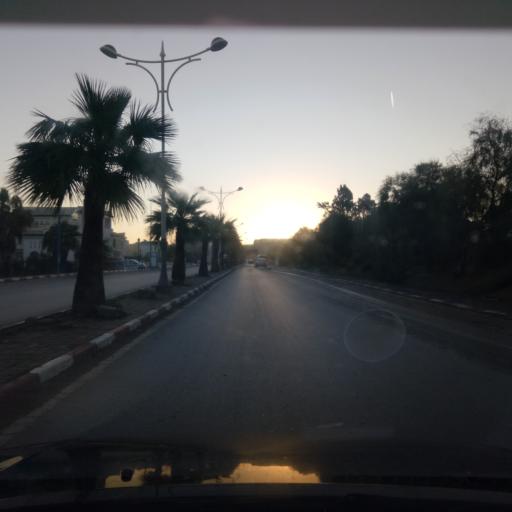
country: DZ
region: Tipaza
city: Bou Ismail
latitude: 36.6402
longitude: 2.7019
